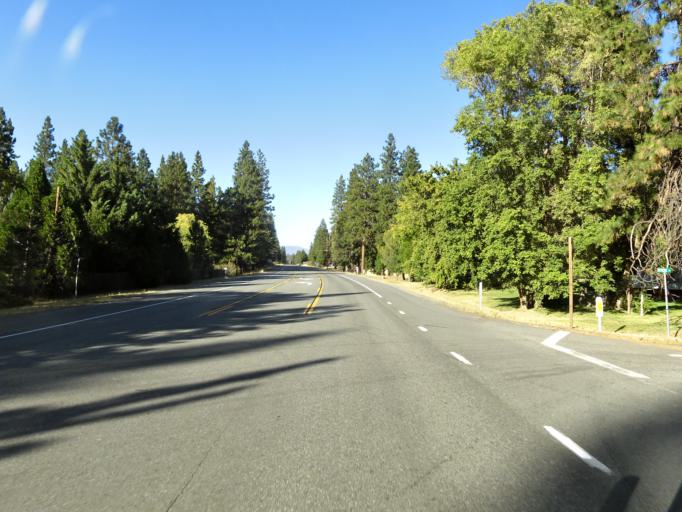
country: US
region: California
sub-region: Siskiyou County
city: Weed
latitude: 41.4484
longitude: -122.3638
